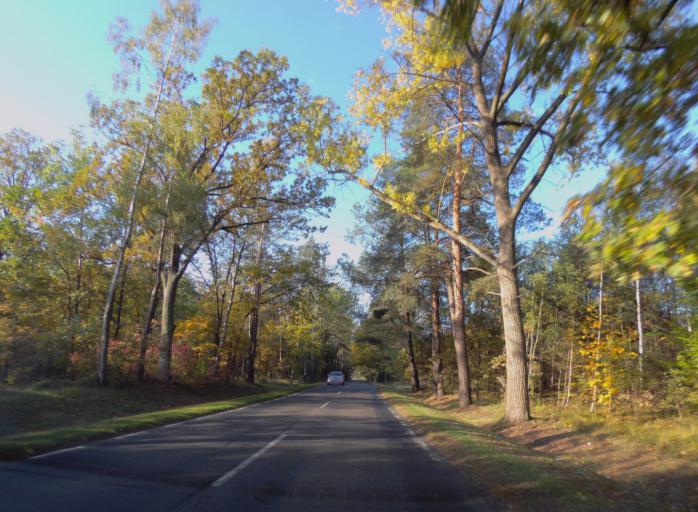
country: PL
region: Masovian Voivodeship
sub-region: Powiat siedlecki
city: Mordy
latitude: 52.1945
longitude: 22.4770
